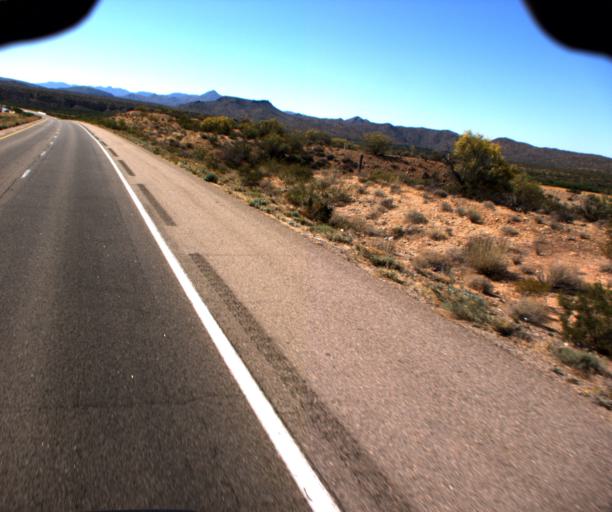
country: US
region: Arizona
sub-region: Yavapai County
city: Bagdad
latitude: 34.6481
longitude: -113.5704
